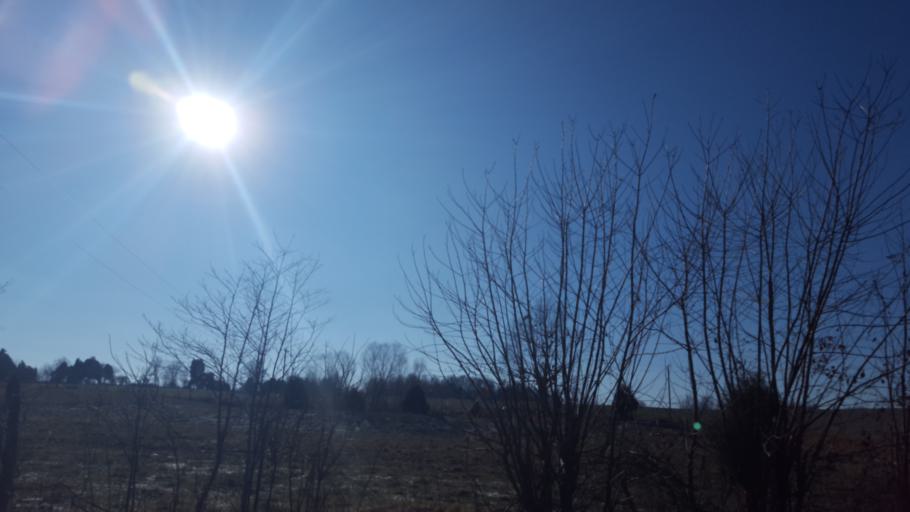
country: US
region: Kentucky
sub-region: Crittenden County
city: Marion
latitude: 37.4200
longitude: -88.0390
